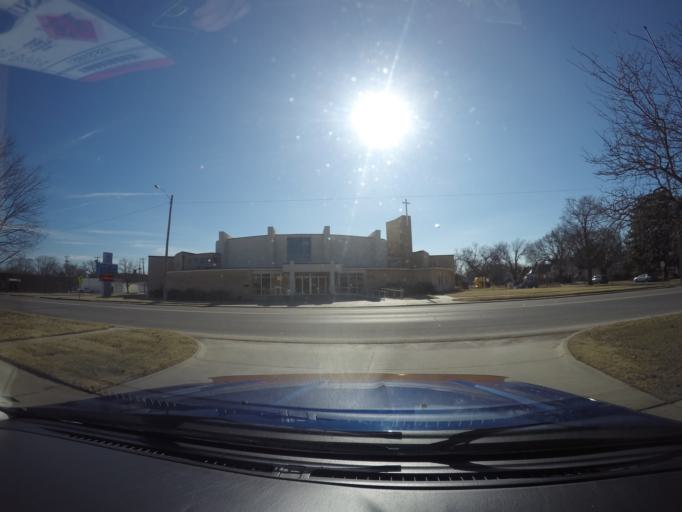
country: US
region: Kansas
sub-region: Sedgwick County
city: Wichita
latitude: 37.6841
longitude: -97.3623
